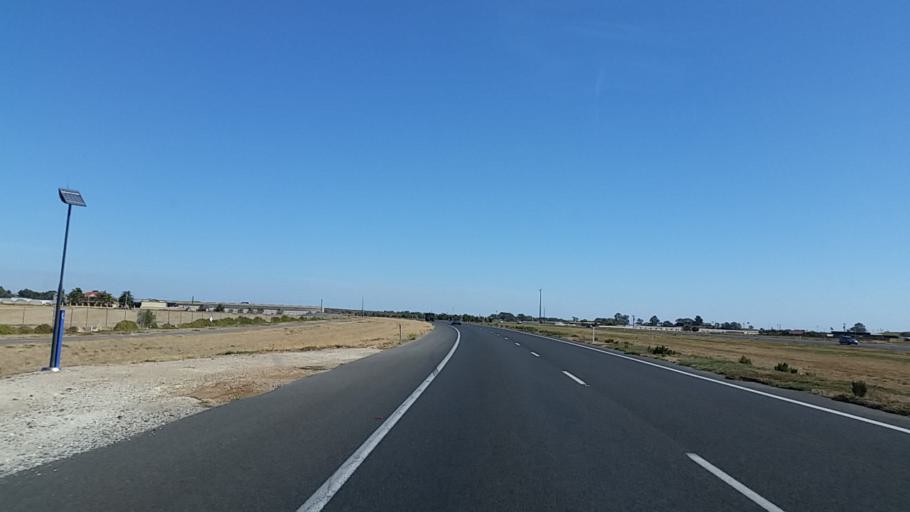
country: AU
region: South Australia
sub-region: Playford
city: Virginia
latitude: -34.6959
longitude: 138.5809
